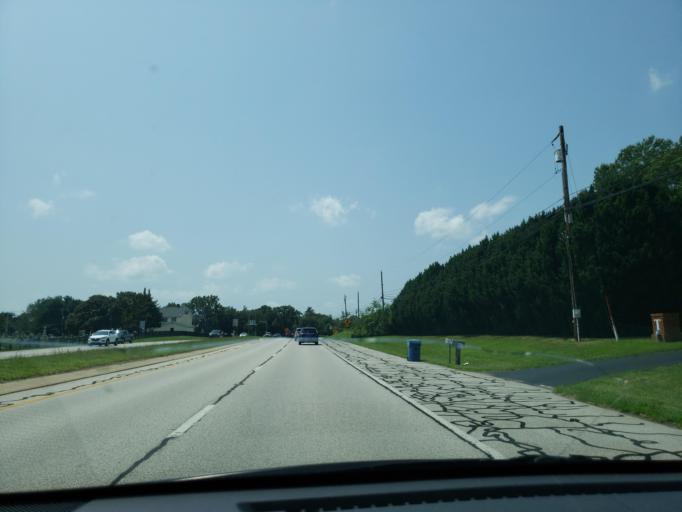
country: US
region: Delaware
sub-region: Kent County
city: Camden
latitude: 39.1139
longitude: -75.5320
